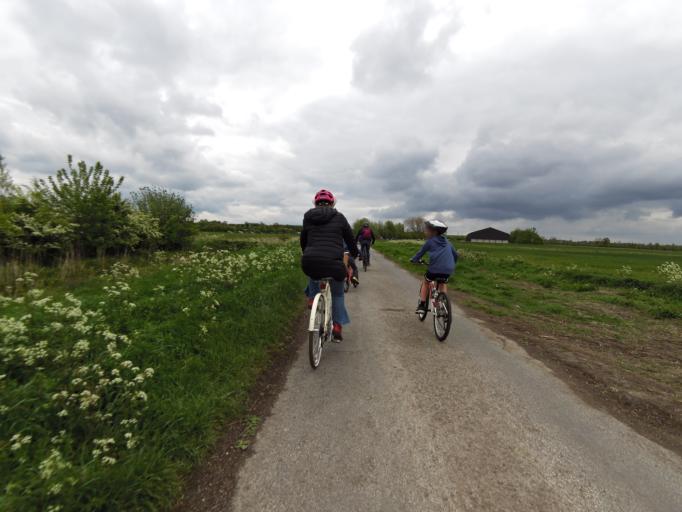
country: GB
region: England
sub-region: Cambridgeshire
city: Bottisham
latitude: 52.2706
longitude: 0.2799
